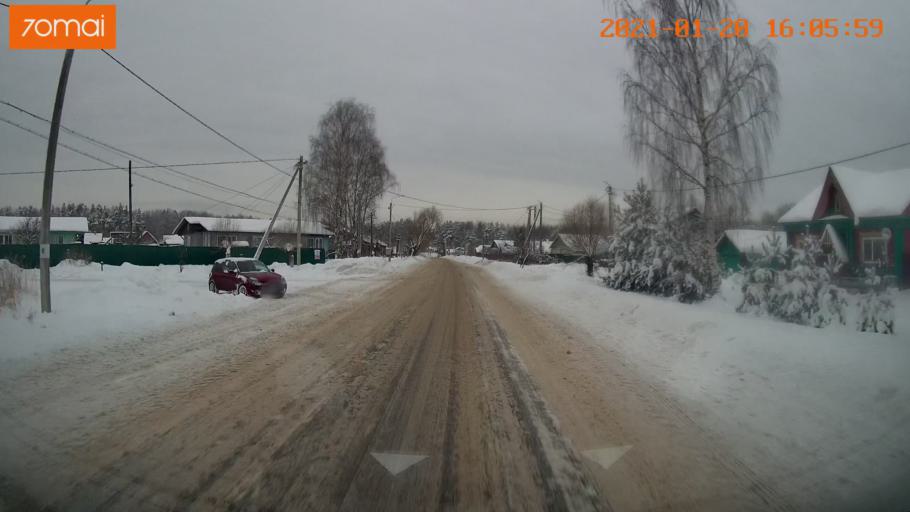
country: RU
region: Vladimir
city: Sudogda
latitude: 56.0685
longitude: 40.7985
